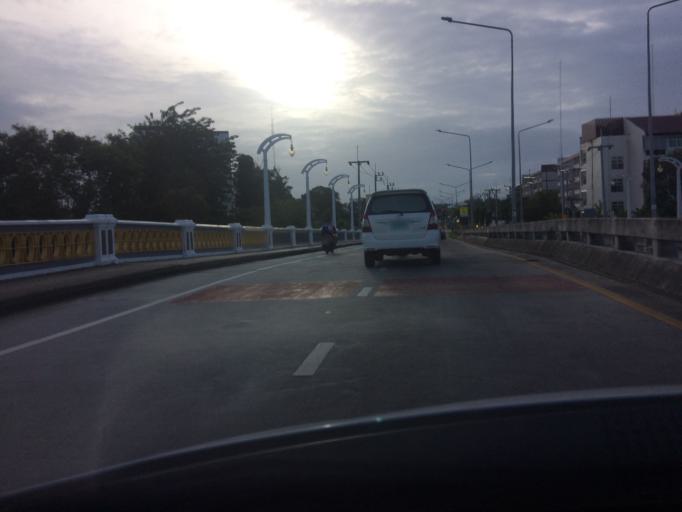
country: TH
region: Phuket
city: Ban Talat Nua
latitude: 7.8691
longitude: 98.3887
